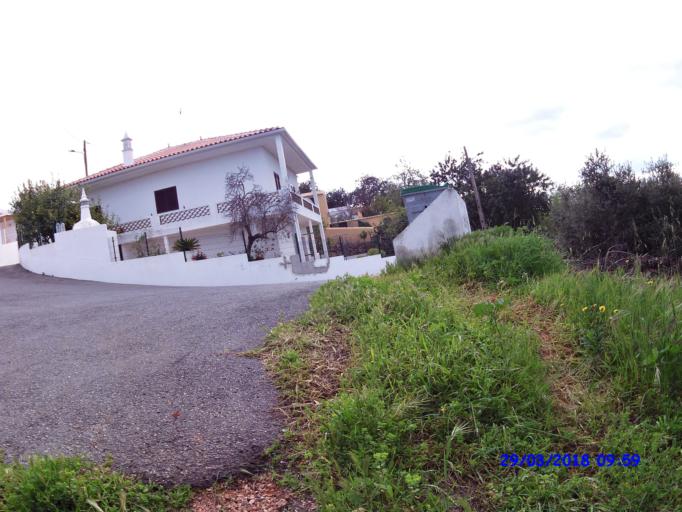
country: PT
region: Faro
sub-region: Loule
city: Boliqueime
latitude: 37.2303
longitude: -8.1640
